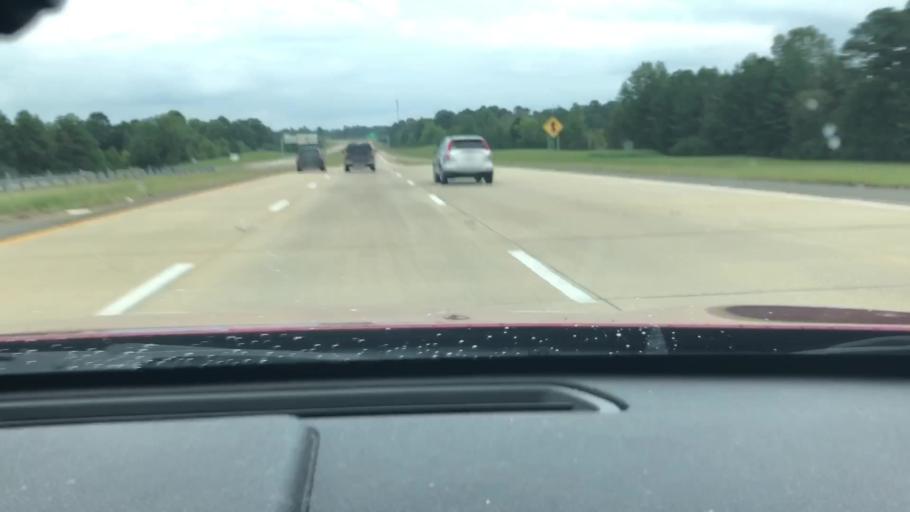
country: US
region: Texas
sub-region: Bowie County
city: Texarkana
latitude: 33.3939
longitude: -94.0134
